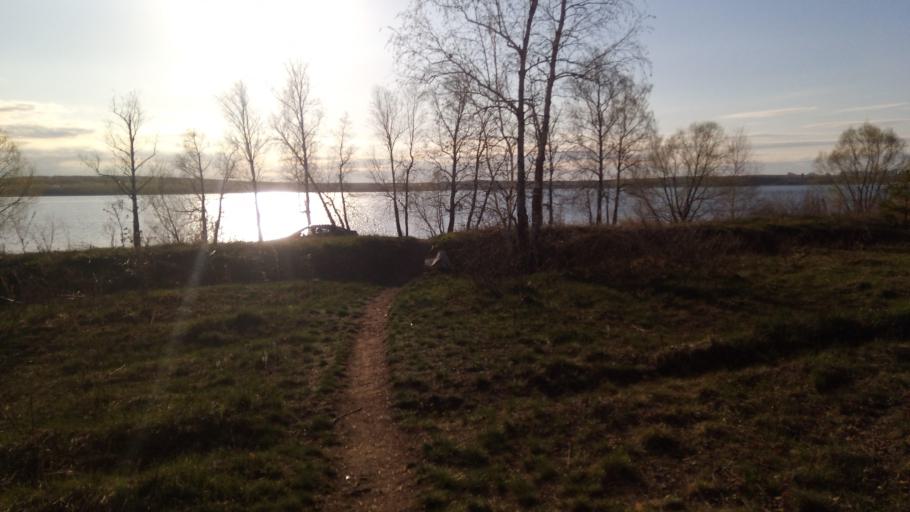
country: RU
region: Chelyabinsk
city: Novosineglazovskiy
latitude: 55.1302
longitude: 61.3289
